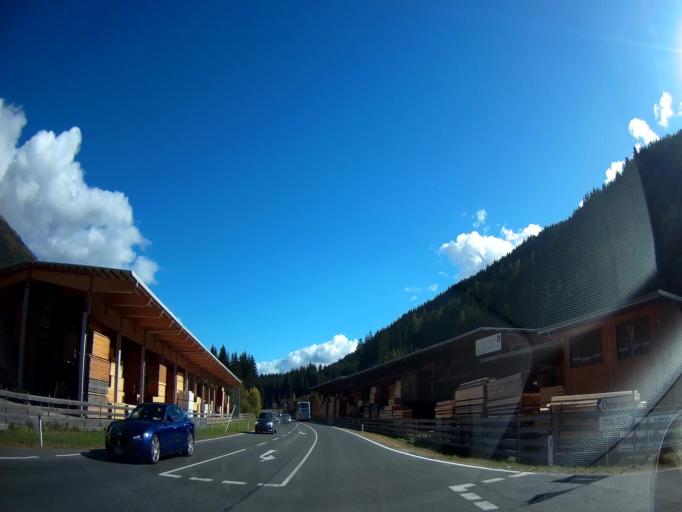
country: AT
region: Tyrol
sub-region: Politischer Bezirk Lienz
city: Sillian
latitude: 46.7407
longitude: 12.3778
